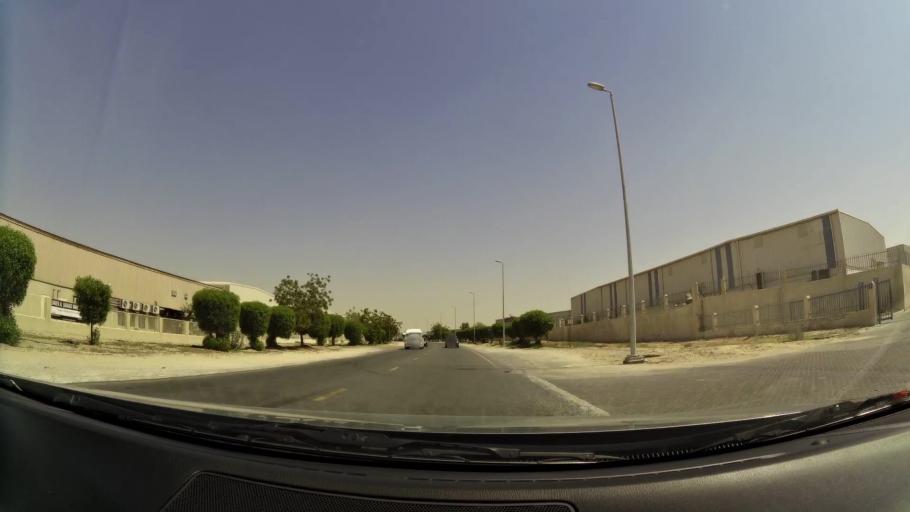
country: AE
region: Dubai
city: Dubai
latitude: 24.9881
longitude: 55.1553
